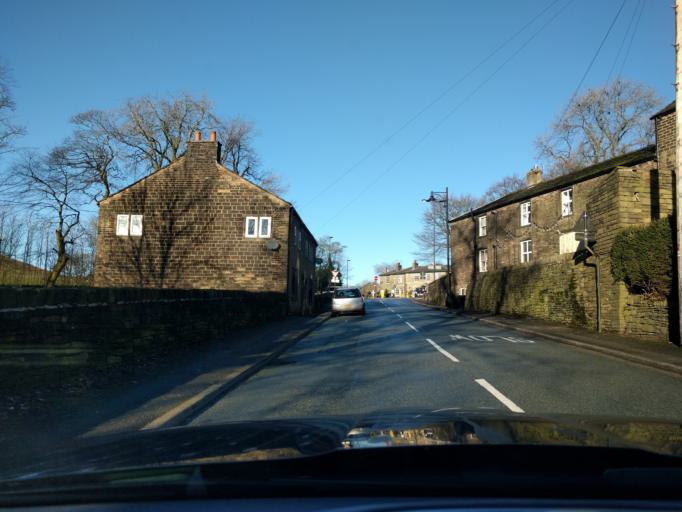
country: GB
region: England
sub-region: Borough of Oldham
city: Delph
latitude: 53.5912
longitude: -2.0396
